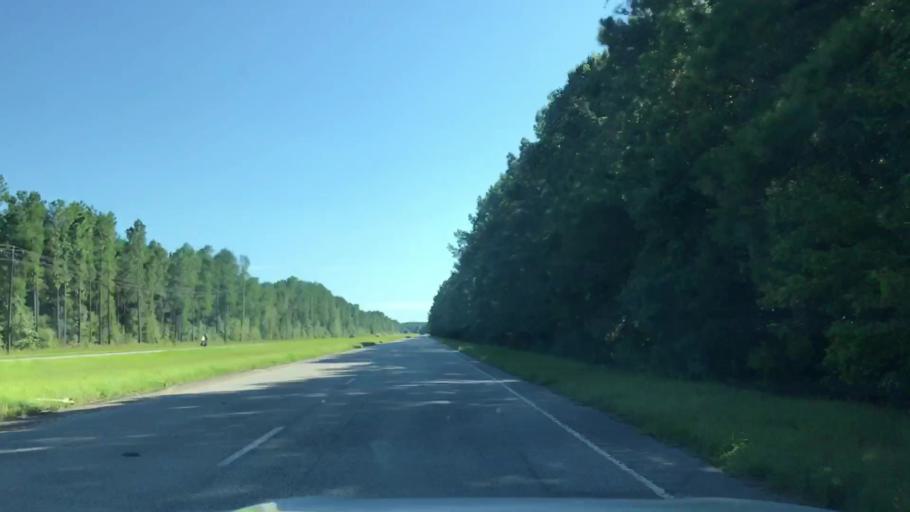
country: US
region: South Carolina
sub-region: Charleston County
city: Awendaw
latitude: 33.0173
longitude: -79.6345
